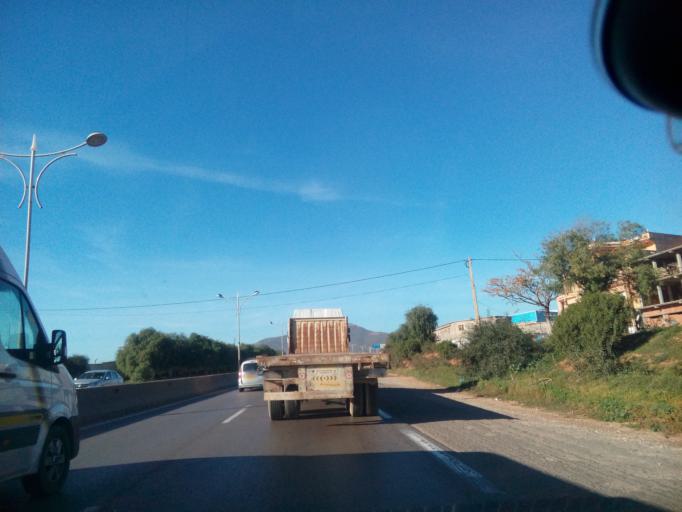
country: DZ
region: Oran
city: Bir el Djir
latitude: 35.7734
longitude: -0.4302
